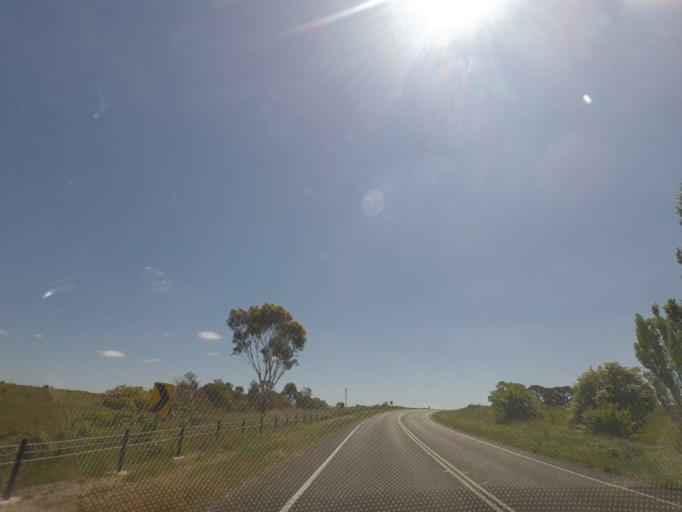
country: AU
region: Victoria
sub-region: Hume
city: Sunbury
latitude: -37.4638
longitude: 144.7422
